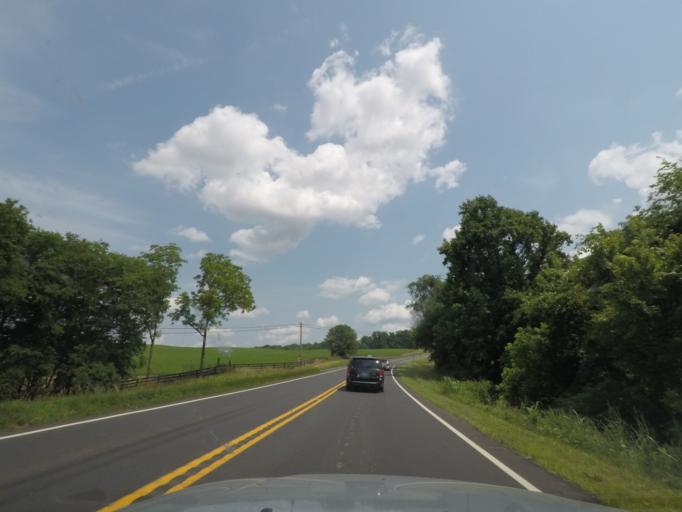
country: US
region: Virginia
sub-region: Orange County
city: Orange
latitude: 38.2735
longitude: -78.1293
